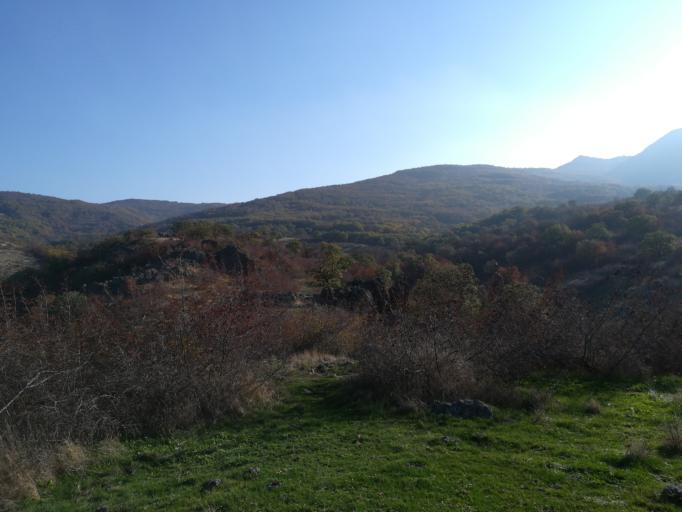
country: BG
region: Khaskovo
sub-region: Obshtina Mineralni Bani
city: Mineralni Bani
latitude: 41.9791
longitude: 25.2385
